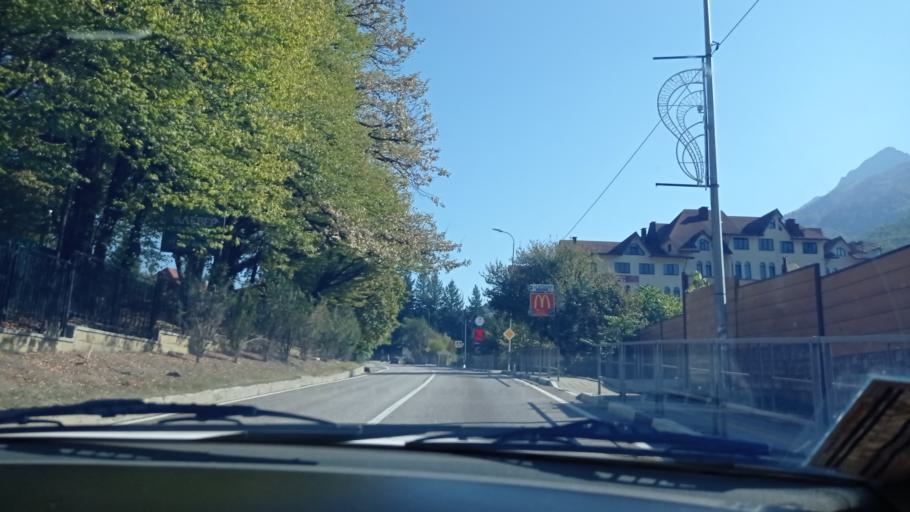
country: RU
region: Krasnodarskiy
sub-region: Sochi City
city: Krasnaya Polyana
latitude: 43.6828
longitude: 40.2164
